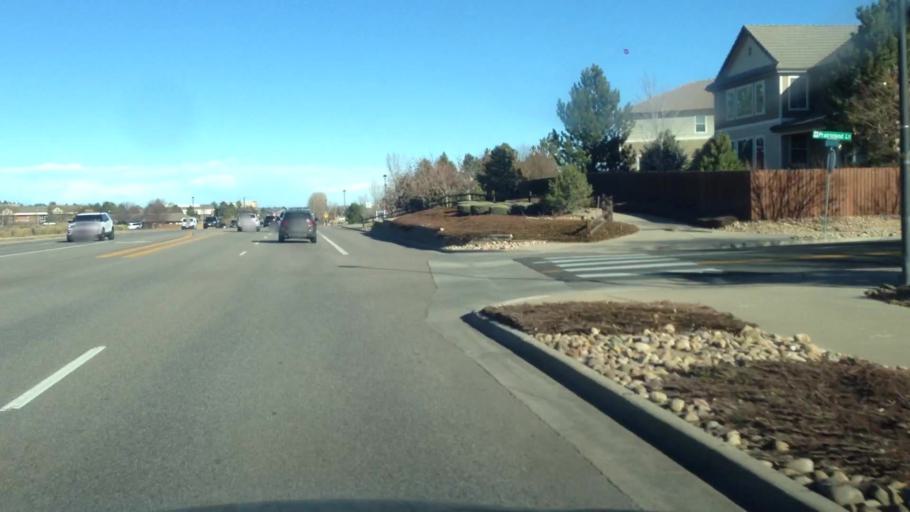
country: US
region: Colorado
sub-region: Douglas County
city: Stonegate
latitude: 39.5287
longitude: -104.7934
